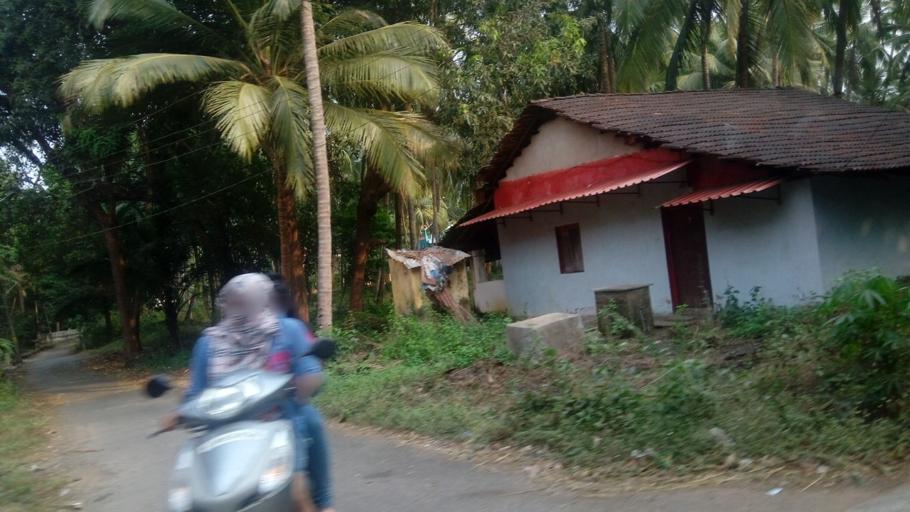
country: IN
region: Goa
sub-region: South Goa
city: Varca
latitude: 15.2280
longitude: 73.9452
